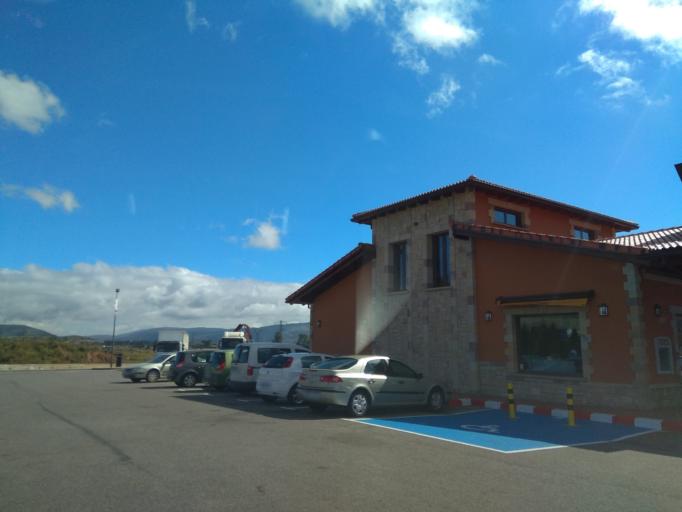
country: ES
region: Cantabria
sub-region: Provincia de Cantabria
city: Reinosa
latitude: 42.9868
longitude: -4.1348
